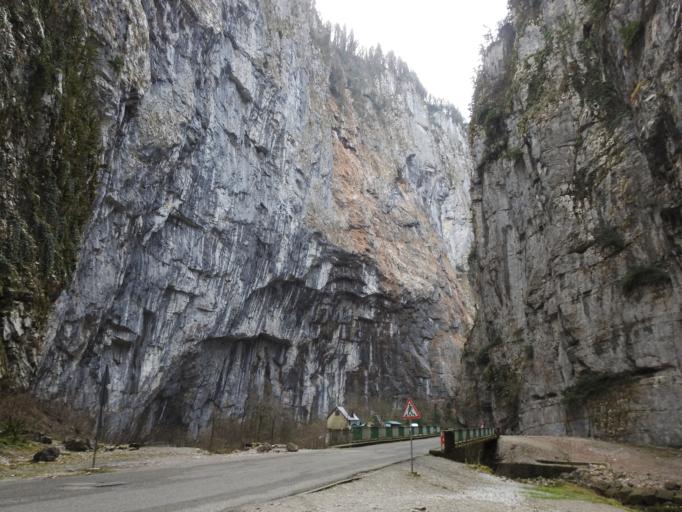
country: GE
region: Abkhazia
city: Gagra
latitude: 43.4272
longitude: 40.5225
